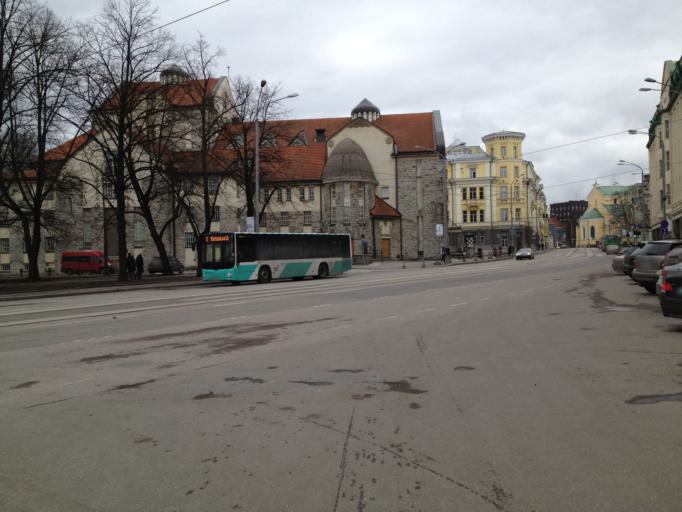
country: EE
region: Harju
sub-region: Tallinna linn
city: Tallinn
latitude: 59.4355
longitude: 24.7492
